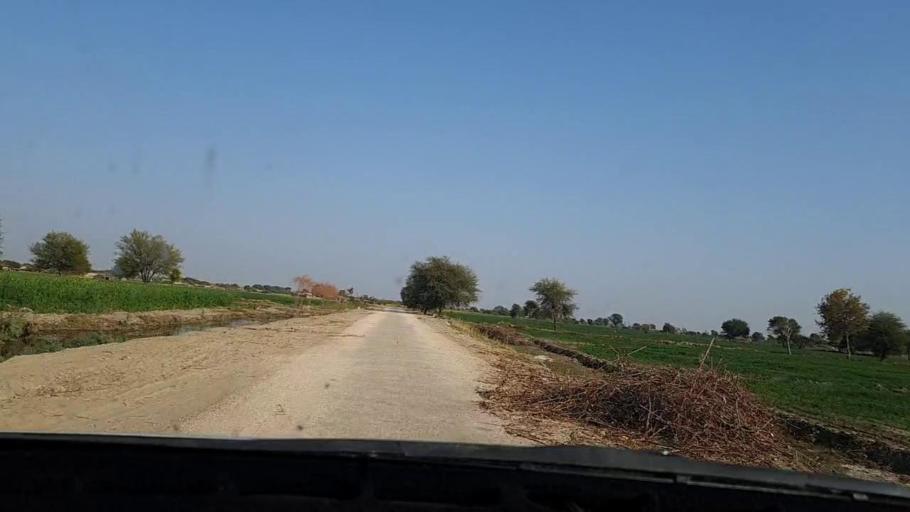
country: PK
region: Sindh
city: Tando Mittha Khan
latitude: 25.8298
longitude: 69.3135
